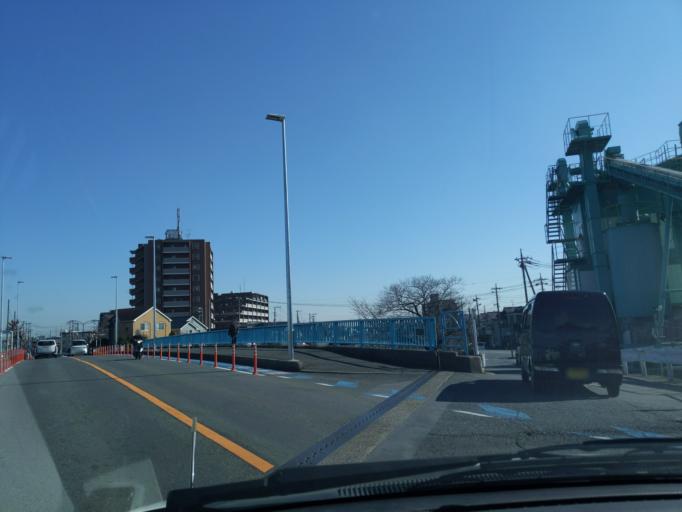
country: JP
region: Saitama
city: Soka
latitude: 35.8281
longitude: 139.8137
